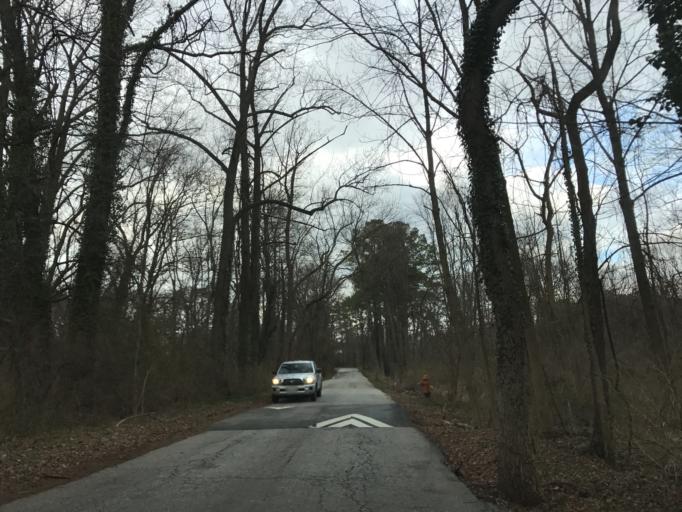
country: US
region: Maryland
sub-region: Baltimore County
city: Lutherville
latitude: 39.4068
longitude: -76.6282
